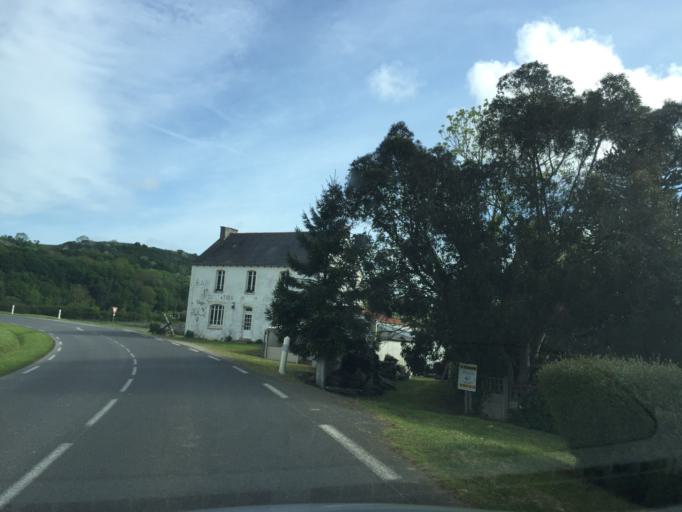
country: FR
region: Brittany
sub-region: Departement des Cotes-d'Armor
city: Matignon
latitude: 48.6181
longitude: -2.3365
